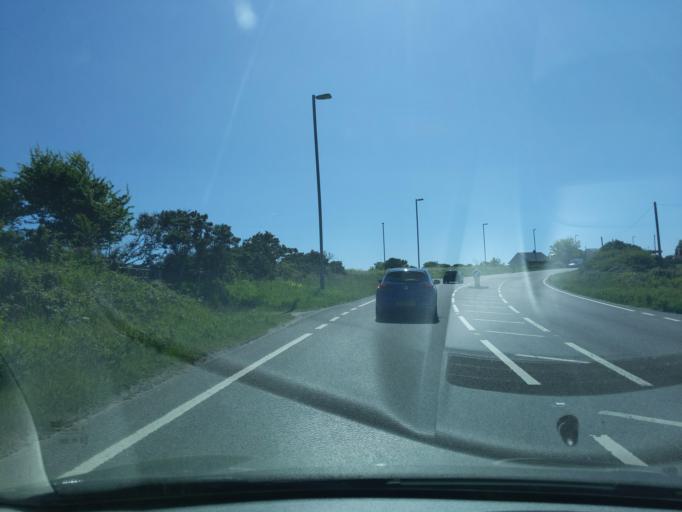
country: GB
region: England
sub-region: Cornwall
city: Penryn
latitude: 50.1643
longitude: -5.1551
